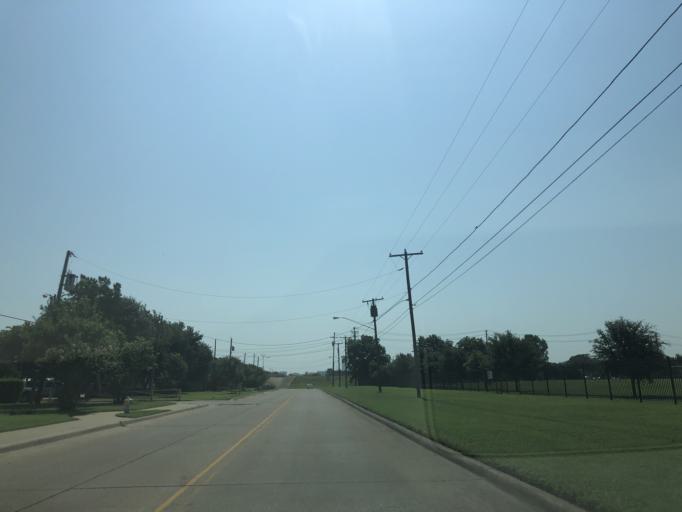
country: US
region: Texas
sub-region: Dallas County
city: Dallas
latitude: 32.7926
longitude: -96.8589
